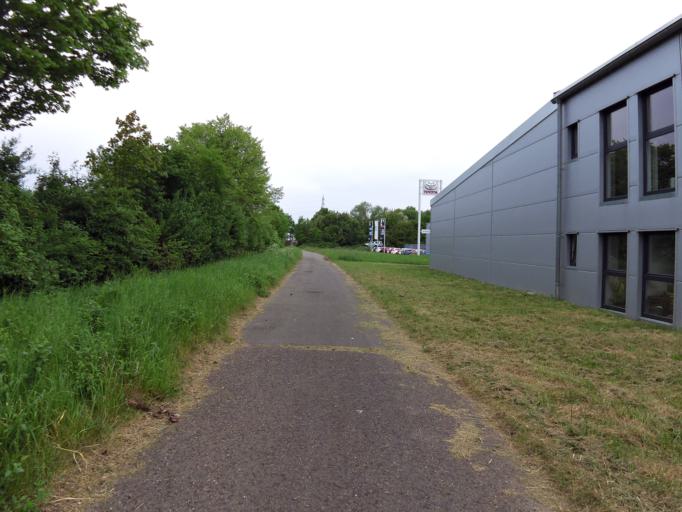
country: DE
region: North Rhine-Westphalia
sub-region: Regierungsbezirk Koln
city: Rheinbach
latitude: 50.6310
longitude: 6.9630
